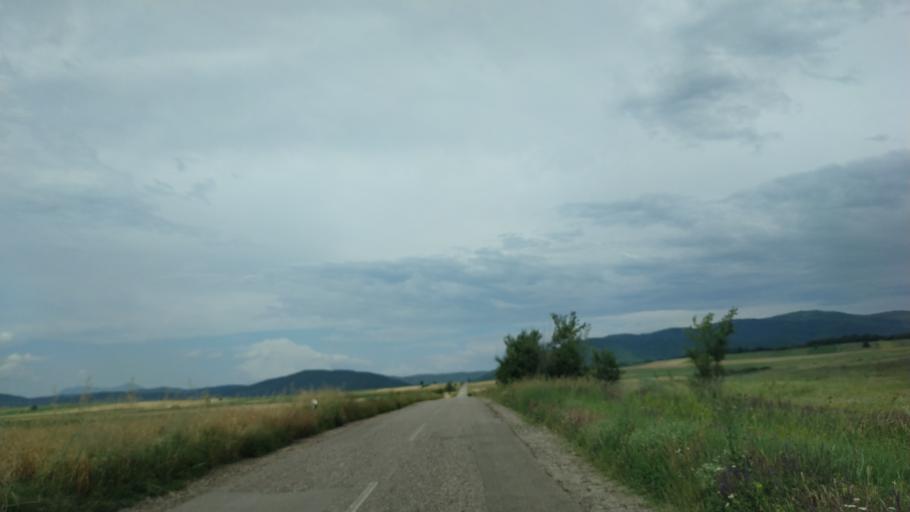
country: RS
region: Central Serbia
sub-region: Nisavski Okrug
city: Aleksinac
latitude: 43.6131
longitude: 21.6592
